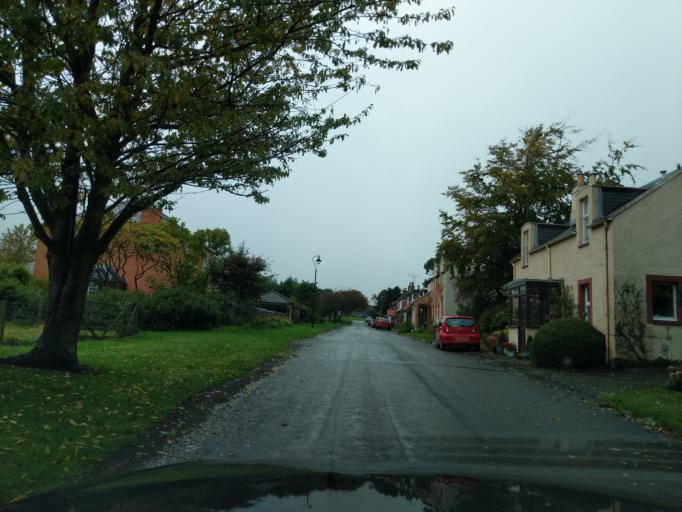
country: GB
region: Scotland
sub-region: East Lothian
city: Dunbar
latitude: 55.9275
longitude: -2.4150
